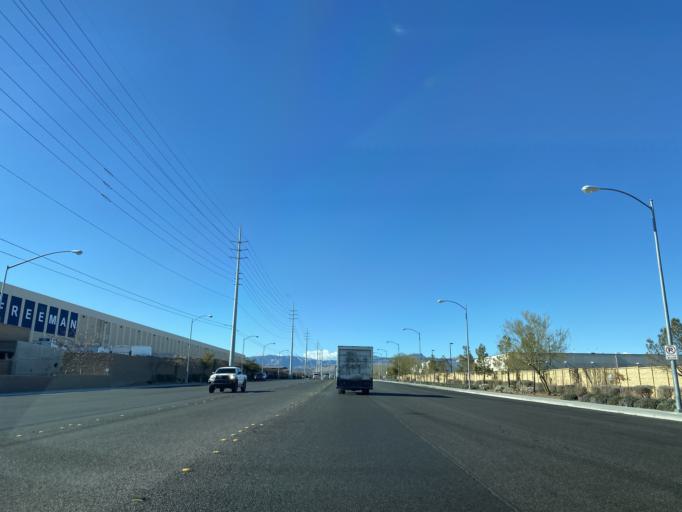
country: US
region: Nevada
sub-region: Clark County
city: Spring Valley
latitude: 36.0708
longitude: -115.2343
